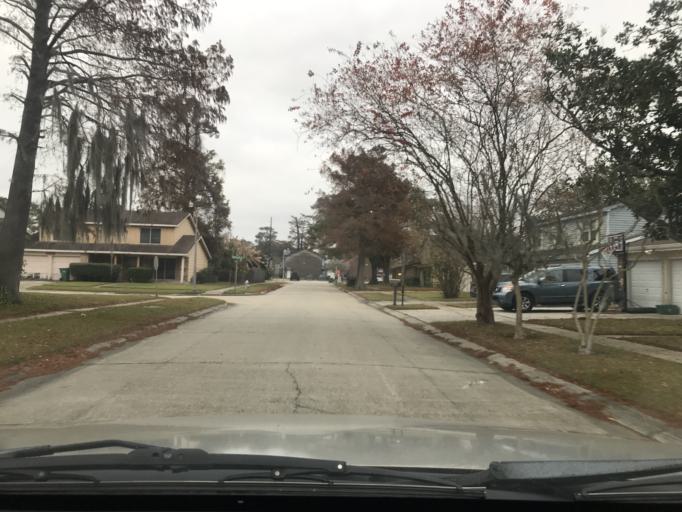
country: US
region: Louisiana
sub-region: Jefferson Parish
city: Woodmere
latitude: 29.8641
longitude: -90.0772
